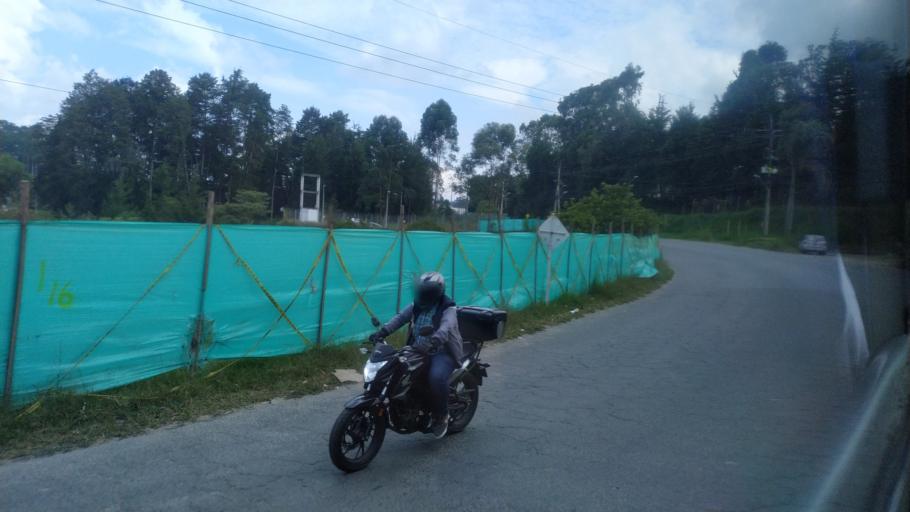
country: CO
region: Antioquia
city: Rionegro
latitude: 6.1719
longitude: -75.3705
